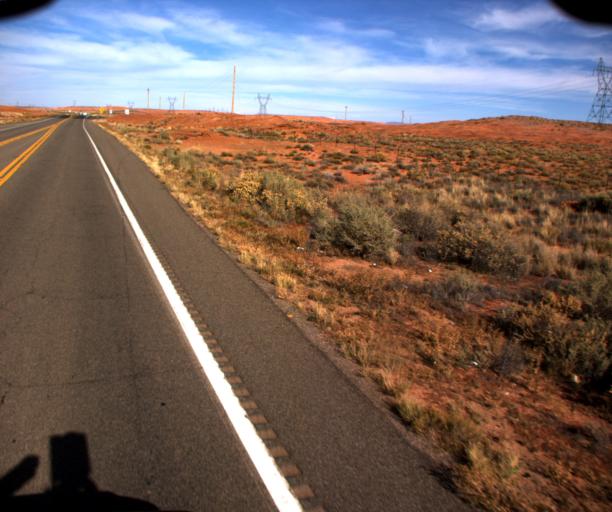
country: US
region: Arizona
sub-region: Navajo County
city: Kayenta
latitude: 36.8361
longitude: -109.8504
